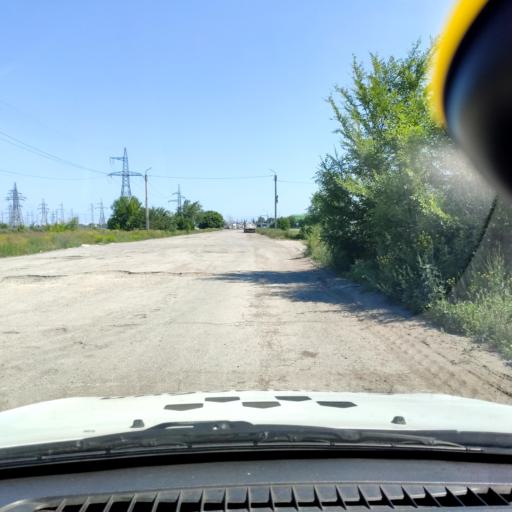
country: RU
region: Samara
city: Zhigulevsk
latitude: 53.5396
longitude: 49.5115
